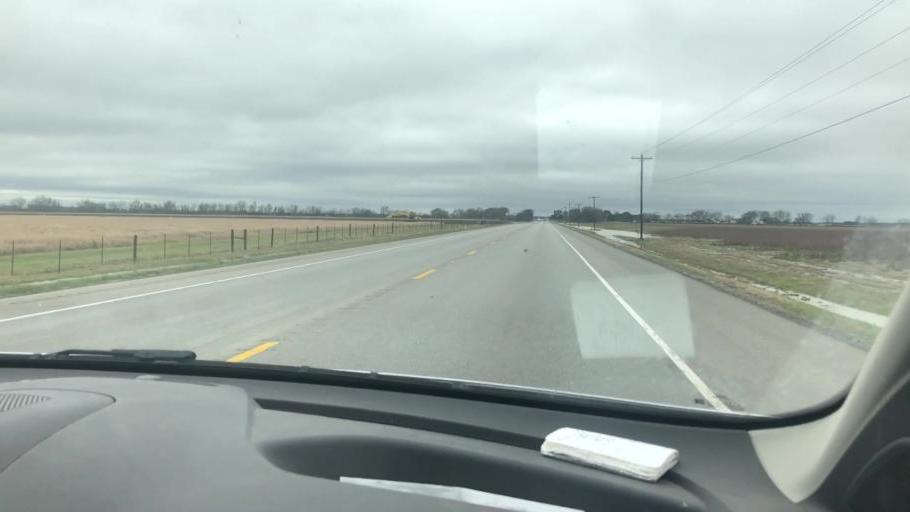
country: US
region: Texas
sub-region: Matagorda County
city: Bay City
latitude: 29.0524
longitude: -95.9708
